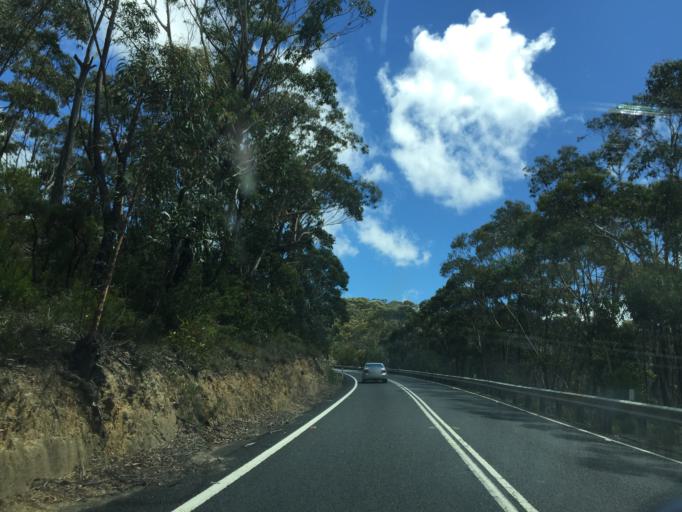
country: AU
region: New South Wales
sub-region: Blue Mountains Municipality
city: Blackheath
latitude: -33.5608
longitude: 150.3718
